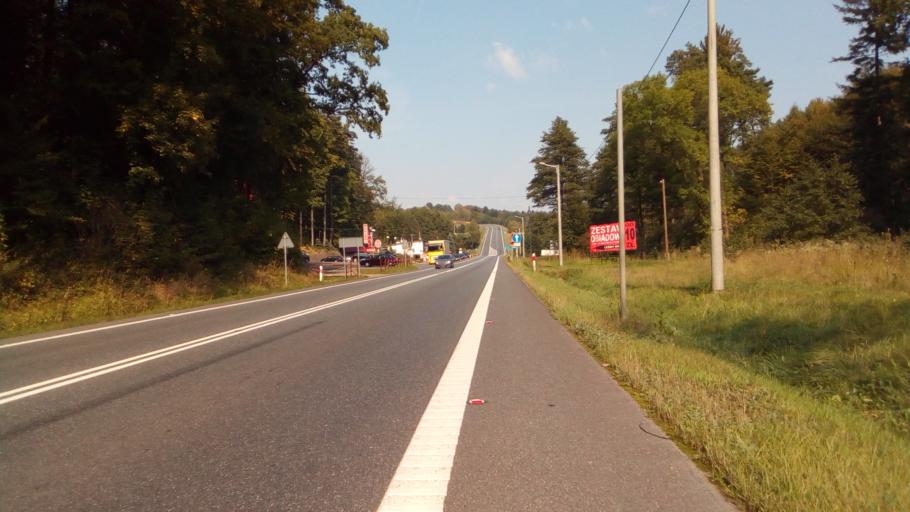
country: PL
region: Subcarpathian Voivodeship
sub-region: Powiat strzyzowski
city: Jawornik
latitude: 49.8298
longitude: 21.8799
